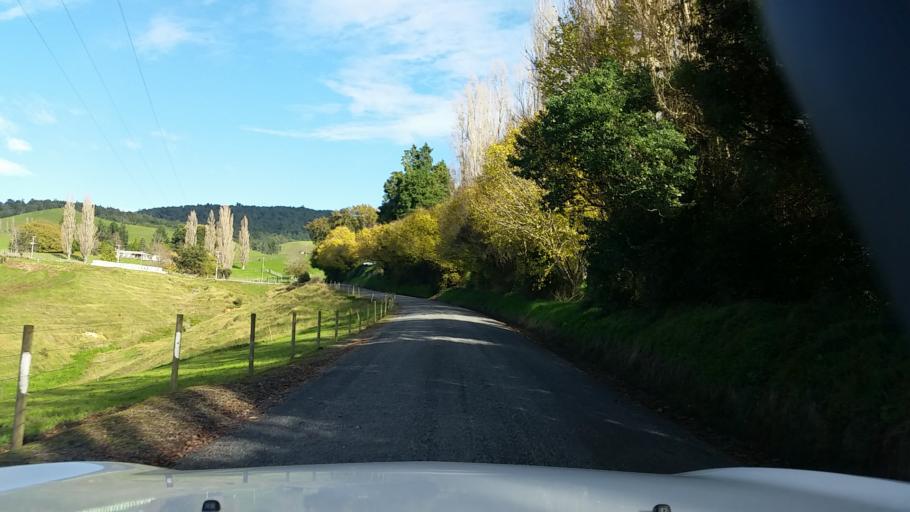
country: NZ
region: Waikato
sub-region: Matamata-Piako District
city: Matamata
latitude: -37.7949
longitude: 175.6345
